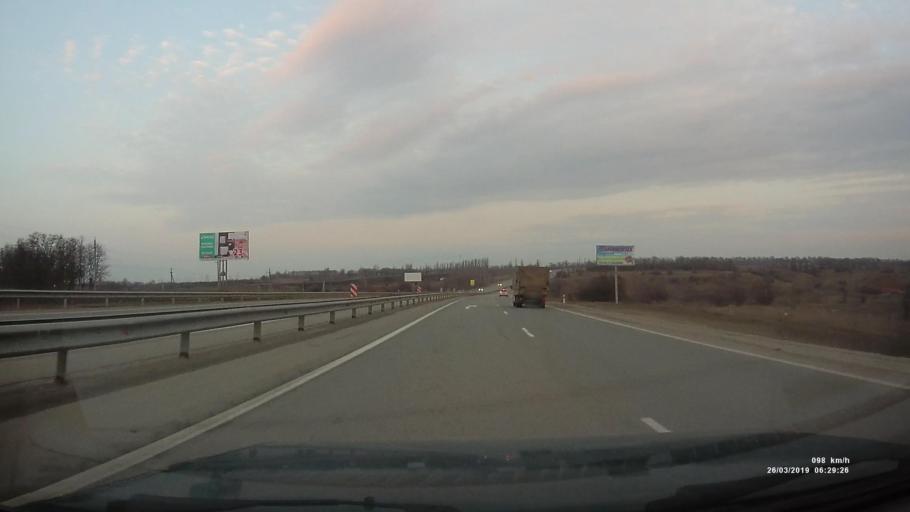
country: RU
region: Rostov
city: Kalinin
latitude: 47.2674
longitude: 39.5719
